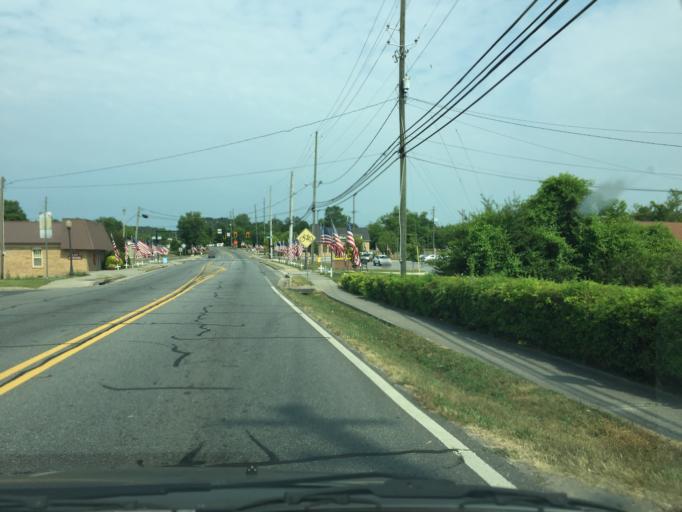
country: US
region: Georgia
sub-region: Catoosa County
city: Ringgold
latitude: 34.9173
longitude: -85.1134
